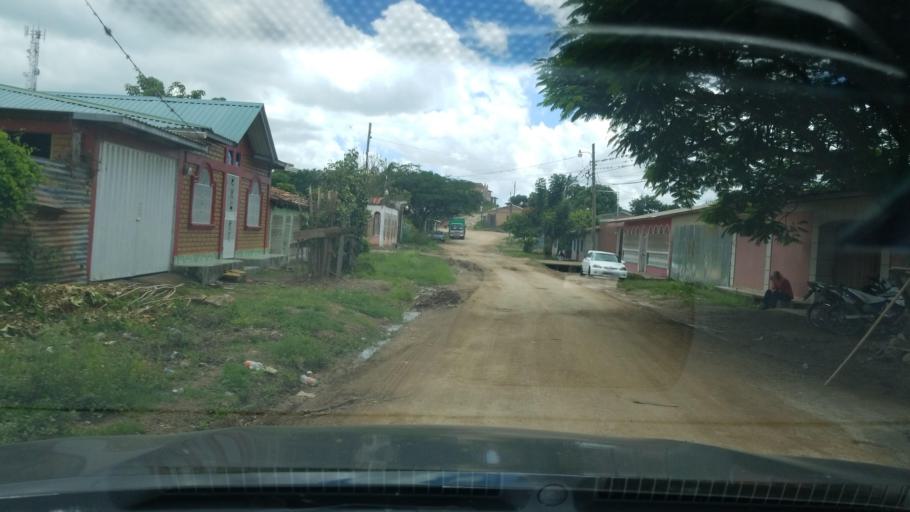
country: HN
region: Francisco Morazan
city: Talanga
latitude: 14.4037
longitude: -87.0772
